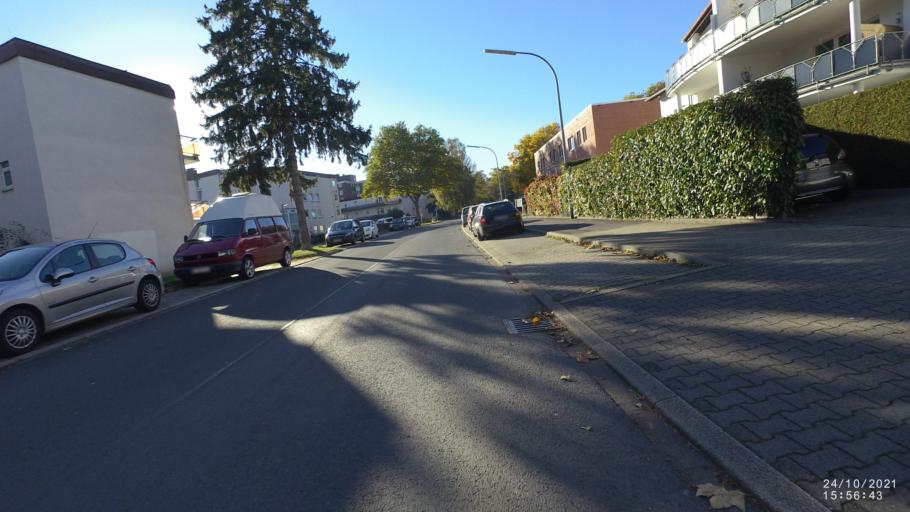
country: DE
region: North Rhine-Westphalia
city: Hemer
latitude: 51.3873
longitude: 7.7581
